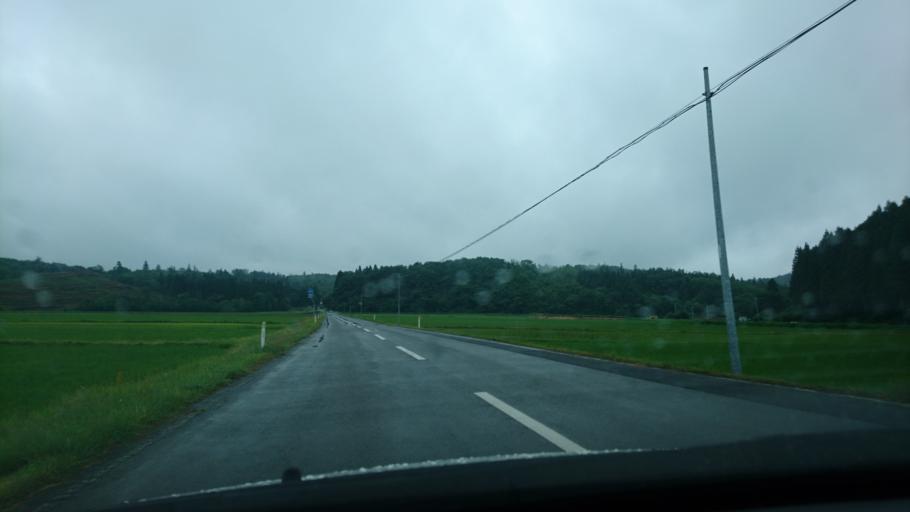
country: JP
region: Iwate
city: Ichinoseki
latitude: 38.9250
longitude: 141.0239
